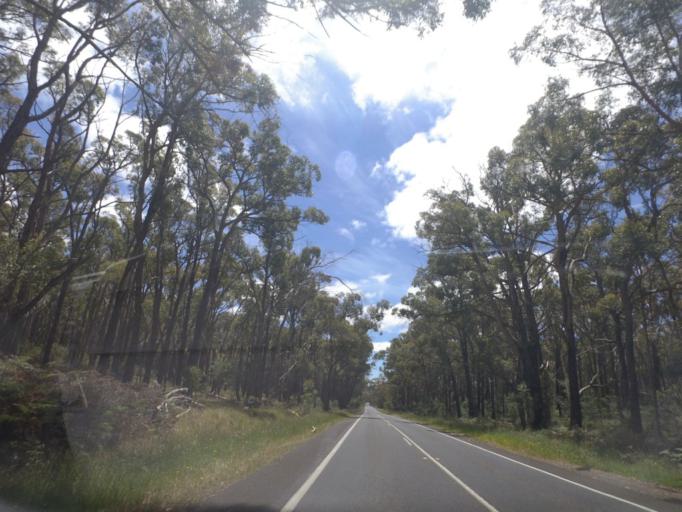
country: AU
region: Victoria
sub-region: Mount Alexander
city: Castlemaine
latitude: -37.3081
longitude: 144.1649
